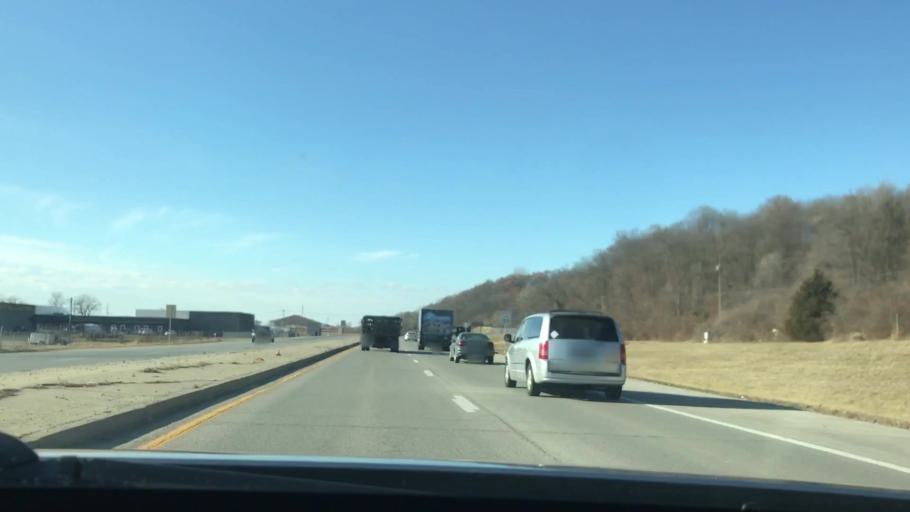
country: US
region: Missouri
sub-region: Platte County
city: Riverside
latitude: 39.1767
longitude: -94.6443
